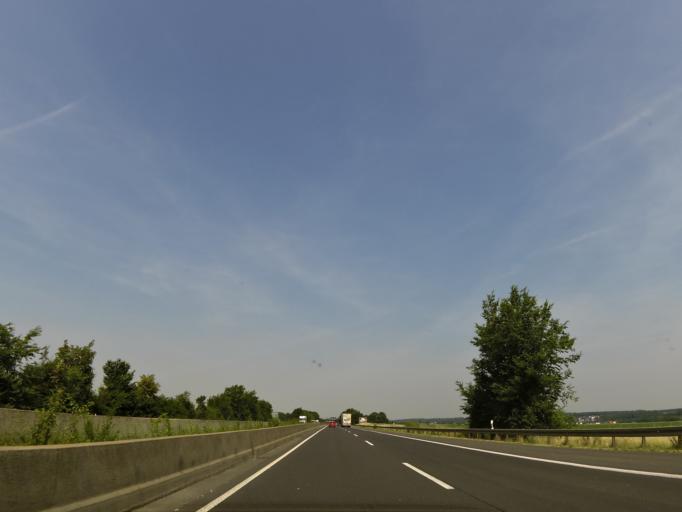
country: DE
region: North Rhine-Westphalia
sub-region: Regierungsbezirk Koln
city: Weilerswist
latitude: 50.7184
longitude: 6.8954
